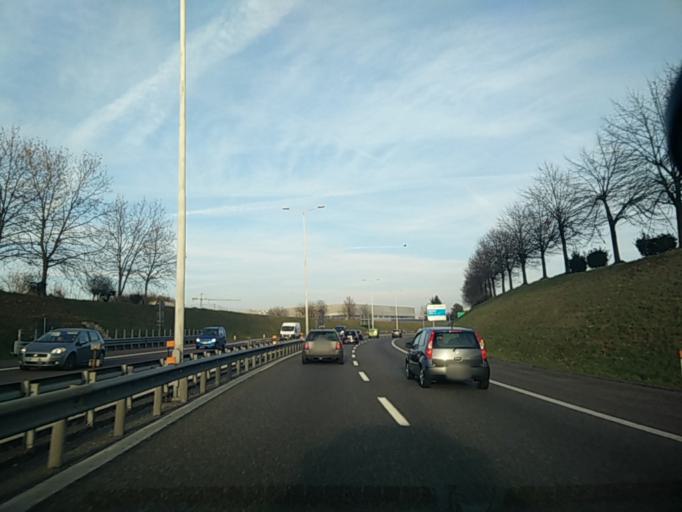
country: IT
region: Lombardy
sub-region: Provincia di Monza e Brianza
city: Nova Milanese
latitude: 45.5751
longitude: 9.2024
